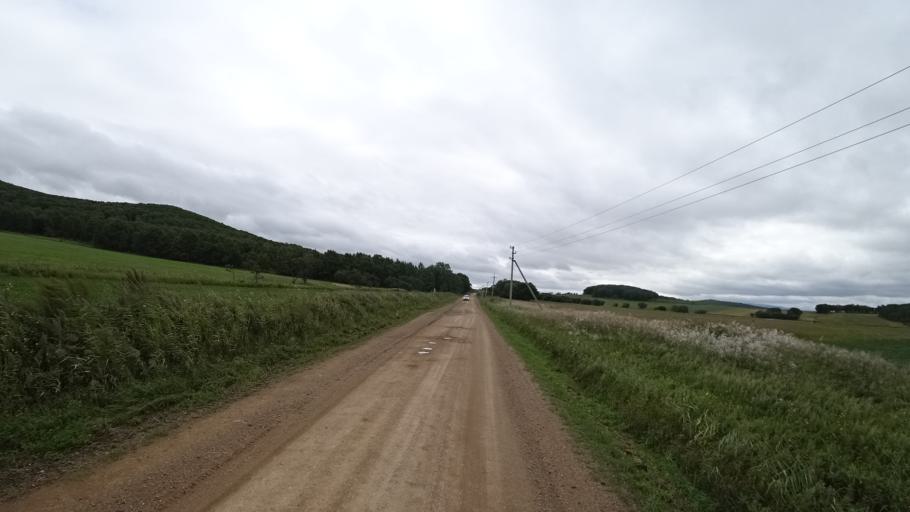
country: RU
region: Primorskiy
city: Chernigovka
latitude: 44.4702
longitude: 132.5825
